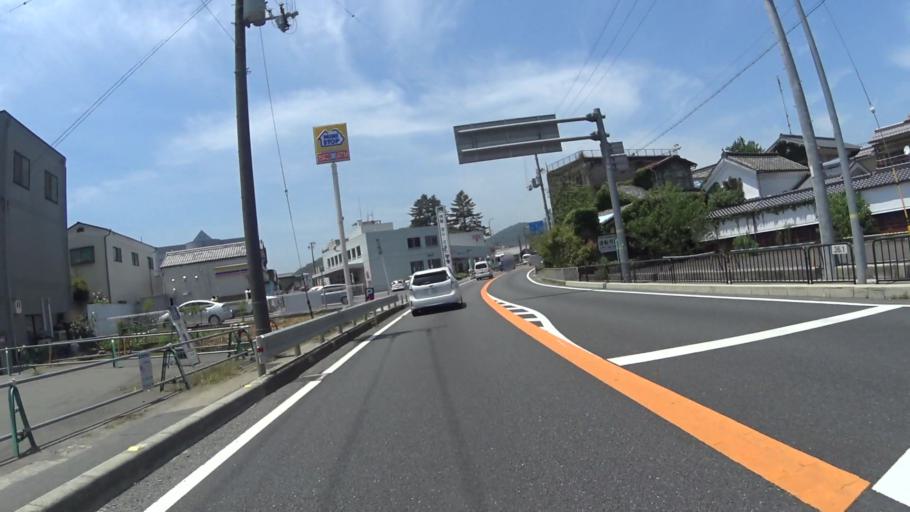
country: JP
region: Kyoto
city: Kameoka
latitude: 35.1098
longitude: 135.4719
